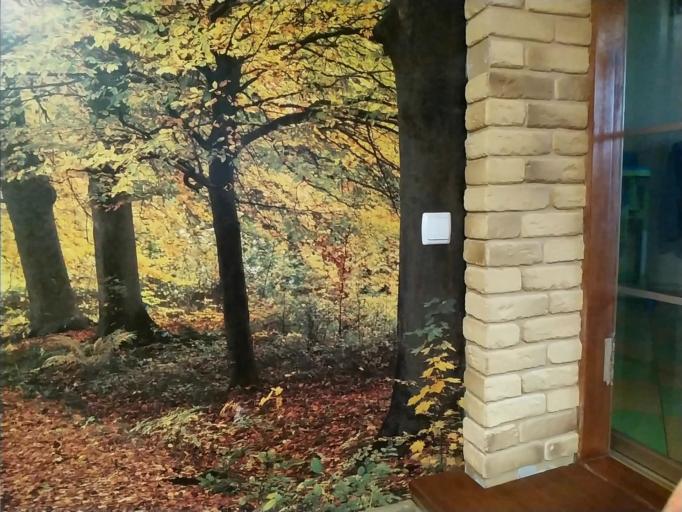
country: RU
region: Smolensk
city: Safonovo
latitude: 55.1928
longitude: 33.1166
